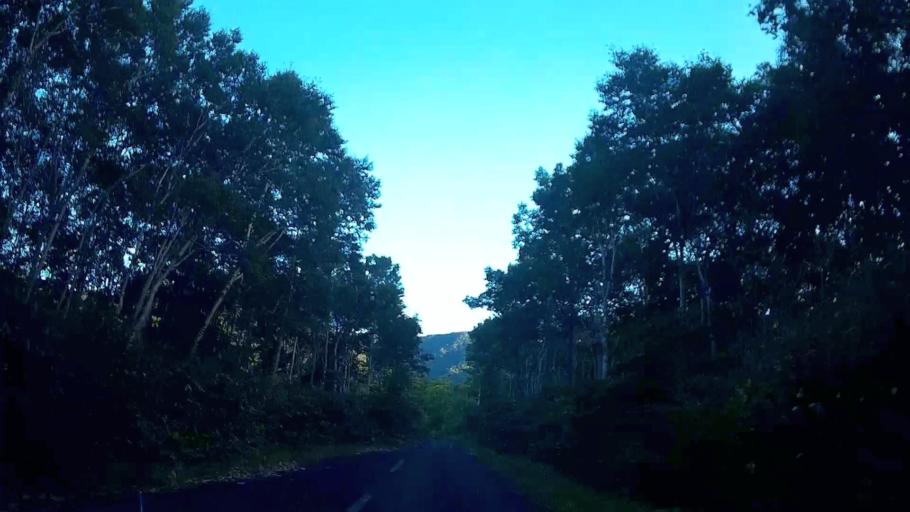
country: JP
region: Hokkaido
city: Iwanai
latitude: 42.6012
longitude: 139.9901
